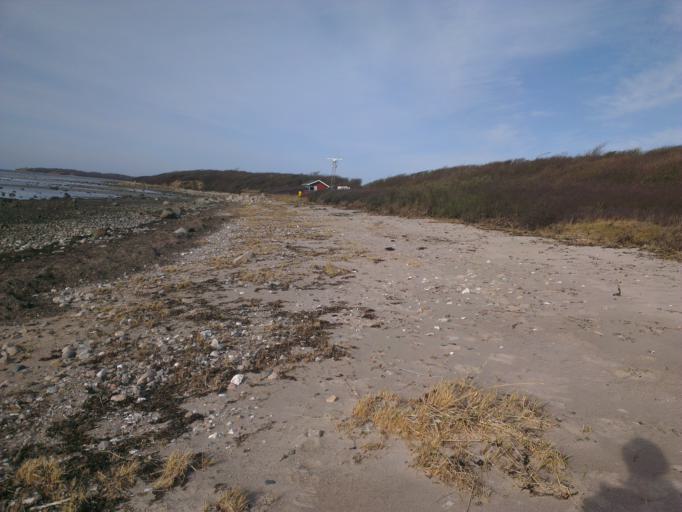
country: DK
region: Capital Region
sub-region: Frederikssund Kommune
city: Jaegerspris
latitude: 55.8586
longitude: 11.9558
